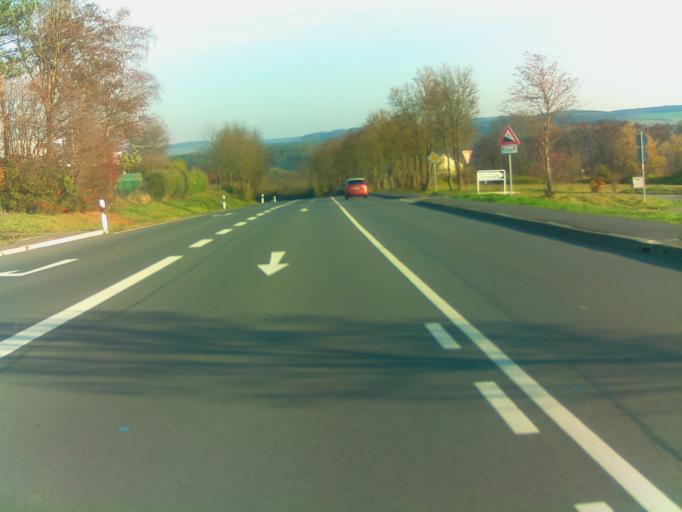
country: DE
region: Baden-Wuerttemberg
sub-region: Regierungsbezirk Stuttgart
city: Wertheim
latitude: 49.7511
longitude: 9.5000
